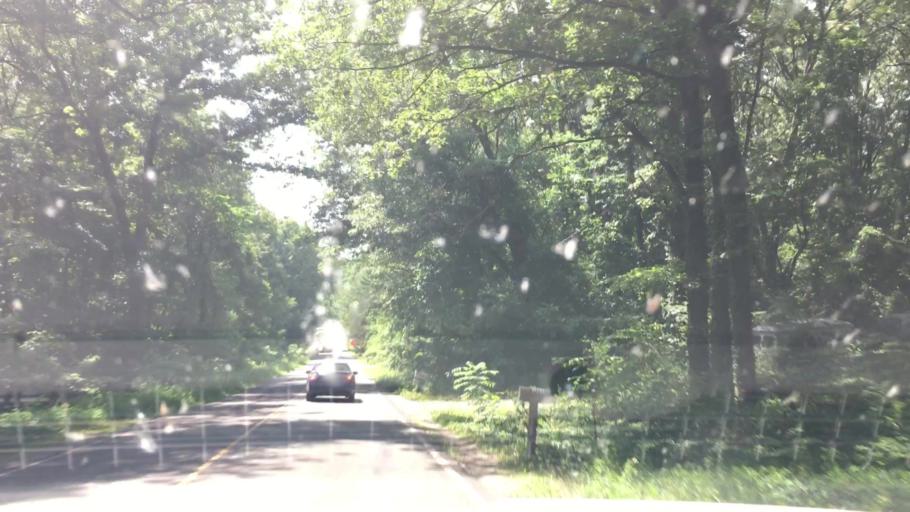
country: US
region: Michigan
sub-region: Kalamazoo County
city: Parchment
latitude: 42.4290
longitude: -85.5392
